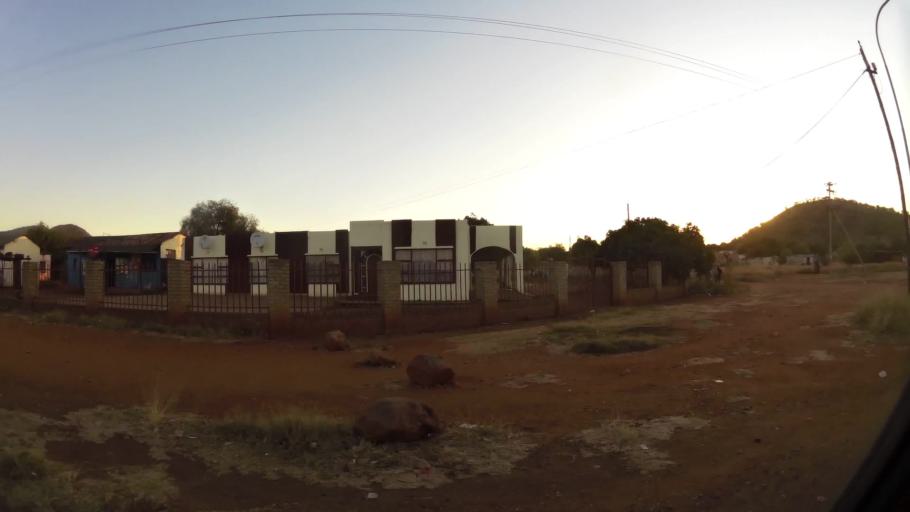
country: ZA
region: North-West
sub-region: Bojanala Platinum District Municipality
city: Rustenburg
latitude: -25.6249
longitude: 27.1974
